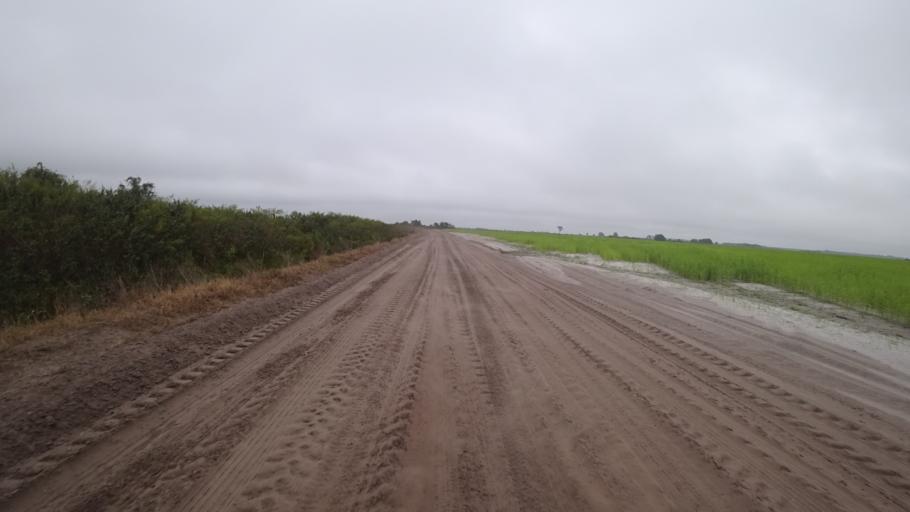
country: US
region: Florida
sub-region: Sarasota County
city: Warm Mineral Springs
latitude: 27.2844
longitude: -82.1656
